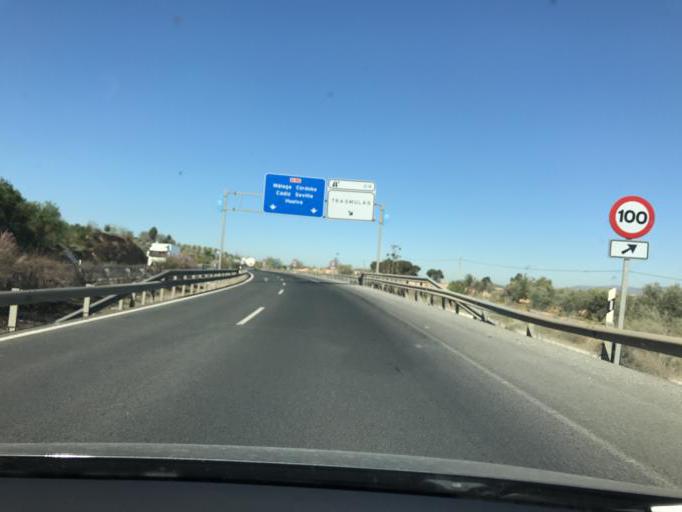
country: ES
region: Andalusia
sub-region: Provincia de Granada
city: Lachar
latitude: 37.1957
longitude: -3.8642
